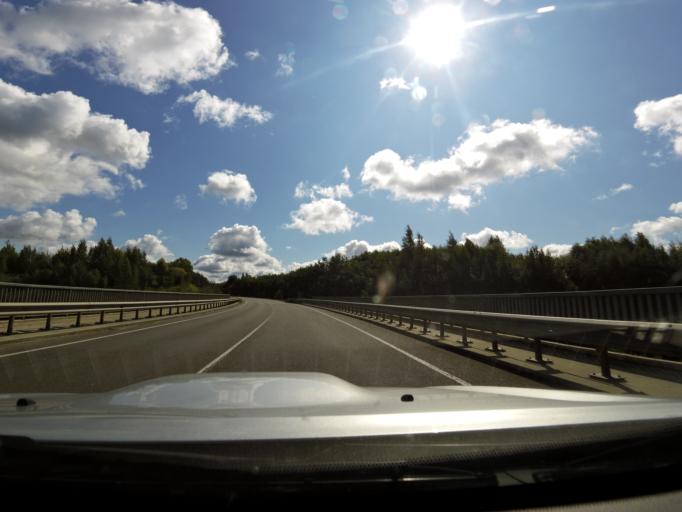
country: LT
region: Utenos apskritis
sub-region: Utena
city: Utena
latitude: 55.4856
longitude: 25.6386
